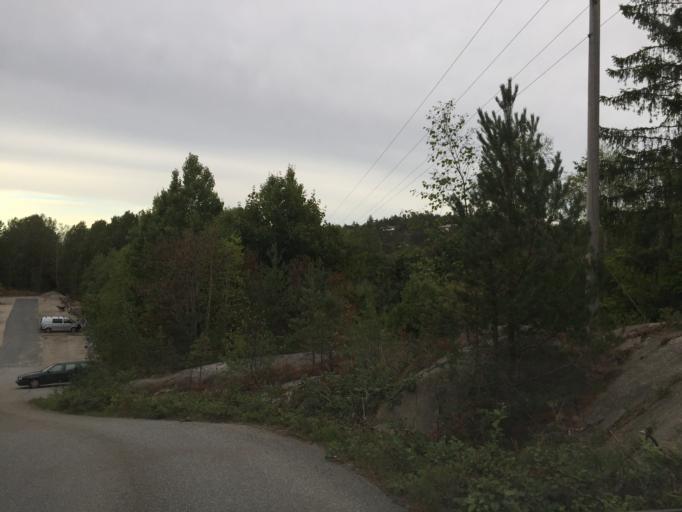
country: NO
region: Ostfold
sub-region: Hvaler
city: Skjaerhalden
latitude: 59.0831
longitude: 10.9996
